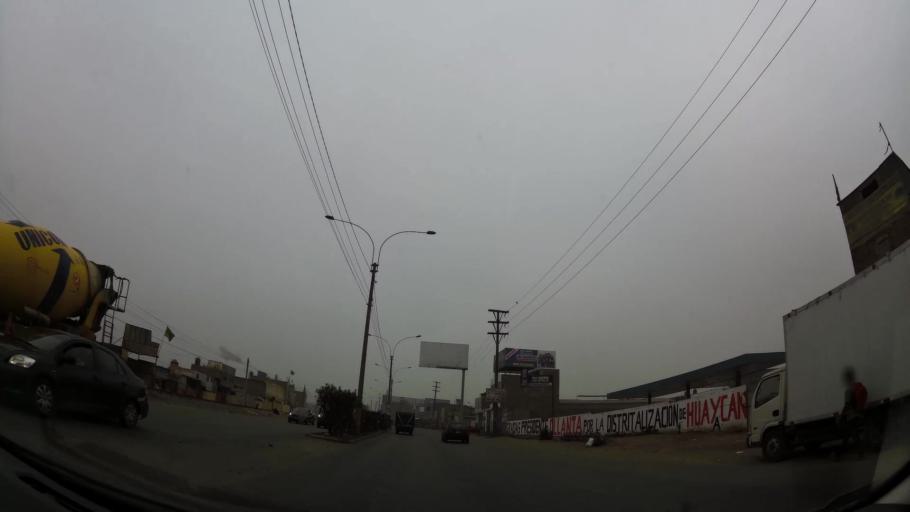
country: PE
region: Lima
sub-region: Lima
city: Santa Maria
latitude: -12.0058
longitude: -76.8473
